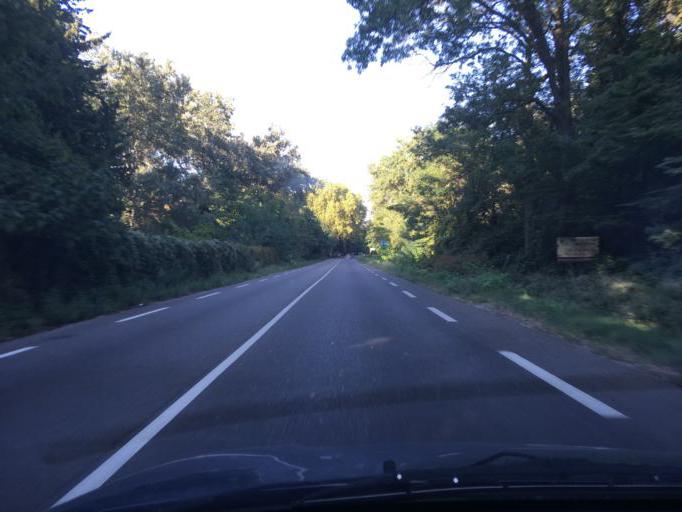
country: FR
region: Languedoc-Roussillon
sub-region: Departement du Gard
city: Remoulins
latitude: 43.9328
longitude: 4.5531
